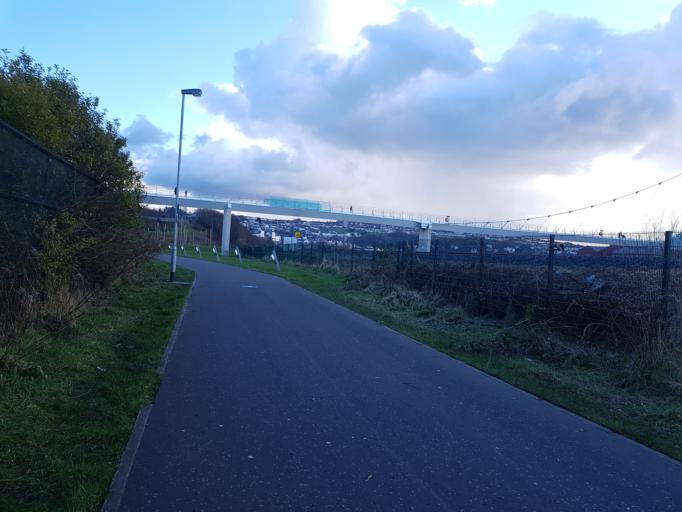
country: GB
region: Northern Ireland
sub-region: City of Derry
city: Derry
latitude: 54.9990
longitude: -7.3144
